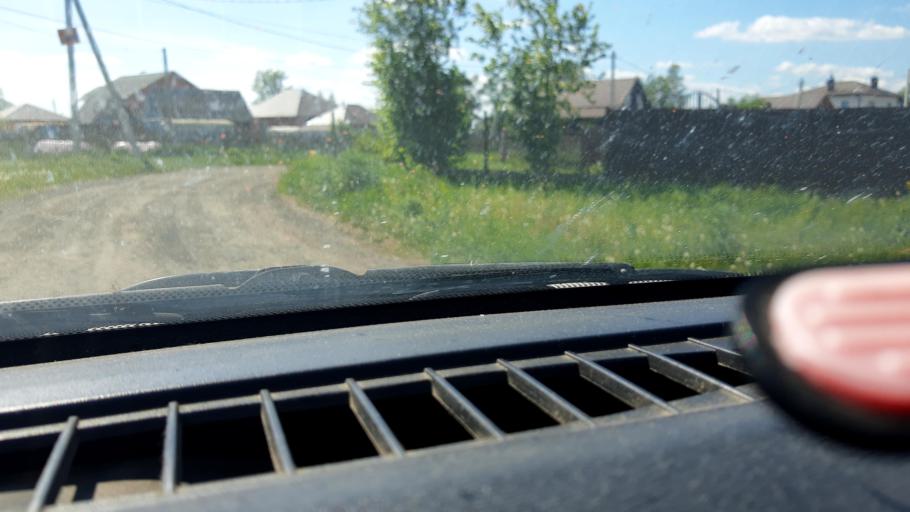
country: RU
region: Bashkortostan
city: Kabakovo
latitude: 54.6837
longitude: 56.1341
